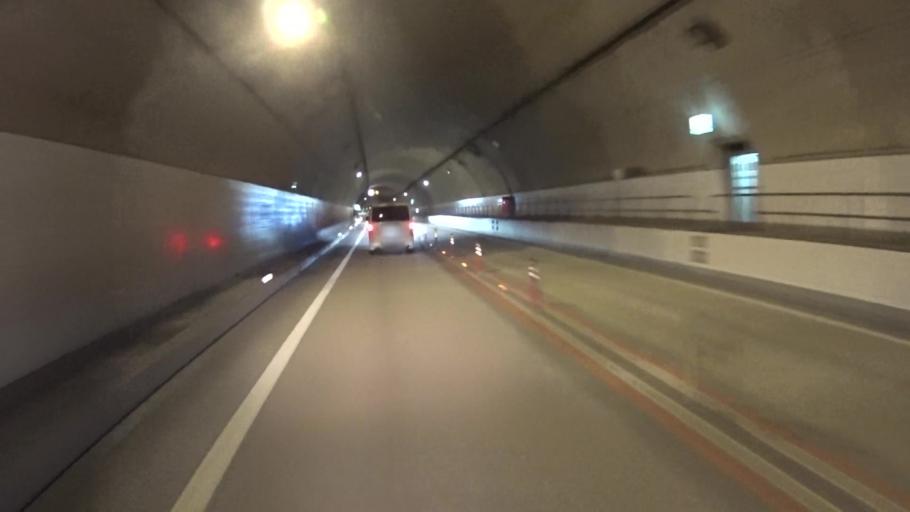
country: JP
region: Kyoto
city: Miyazu
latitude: 35.5356
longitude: 135.1628
